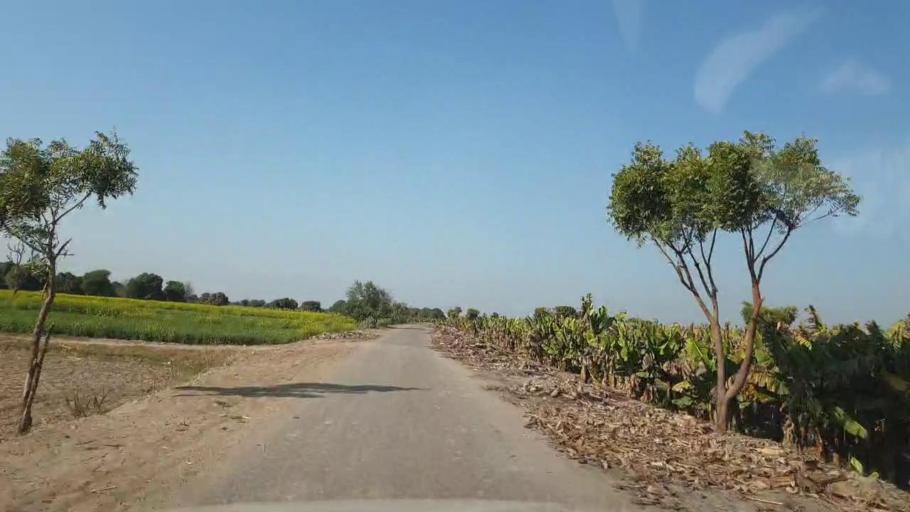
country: PK
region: Sindh
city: Tando Allahyar
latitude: 25.4770
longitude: 68.6604
